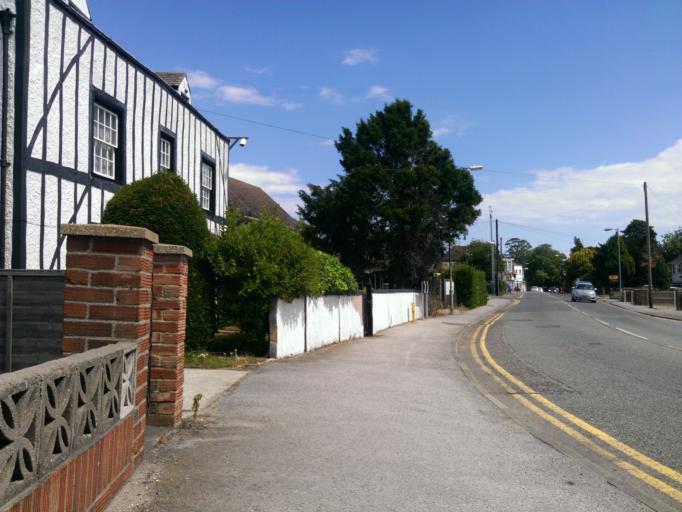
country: GB
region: England
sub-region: Essex
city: Clacton-on-Sea
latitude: 51.8049
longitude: 1.1525
